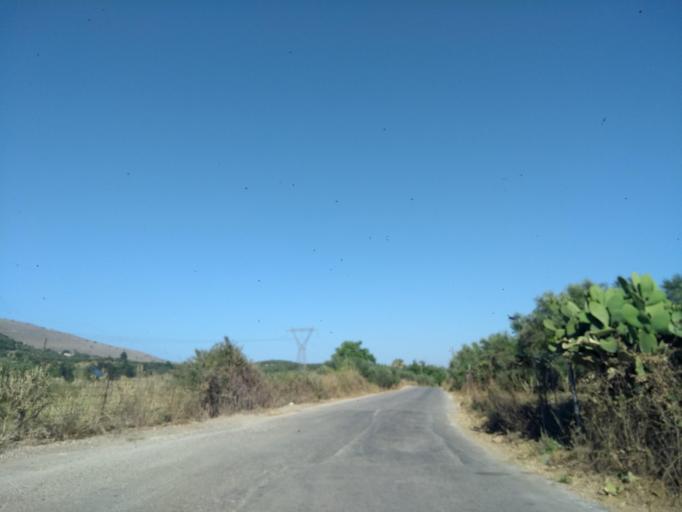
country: GR
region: Crete
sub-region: Nomos Chanias
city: Georgioupolis
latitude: 35.3681
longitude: 24.2303
